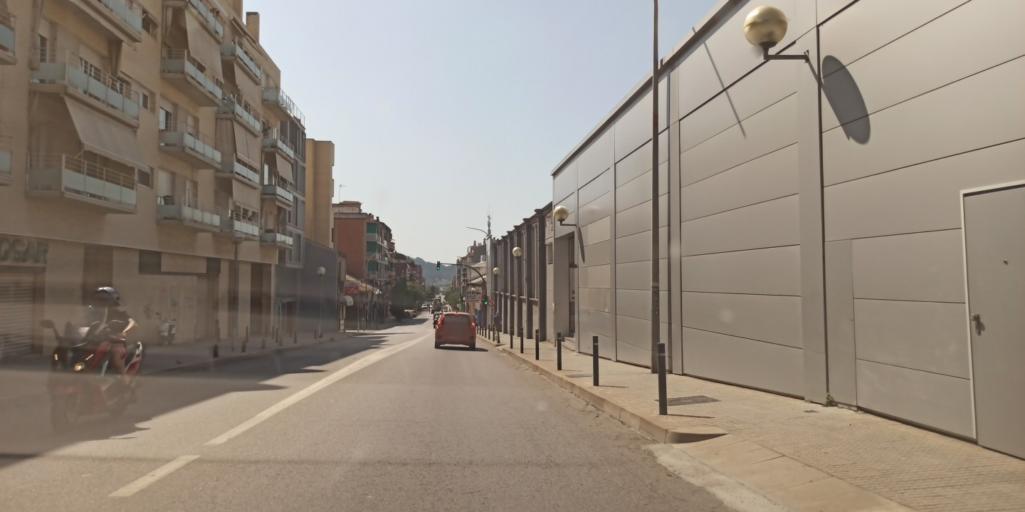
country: ES
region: Catalonia
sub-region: Provincia de Barcelona
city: Cerdanyola del Valles
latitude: 41.4952
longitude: 2.1455
